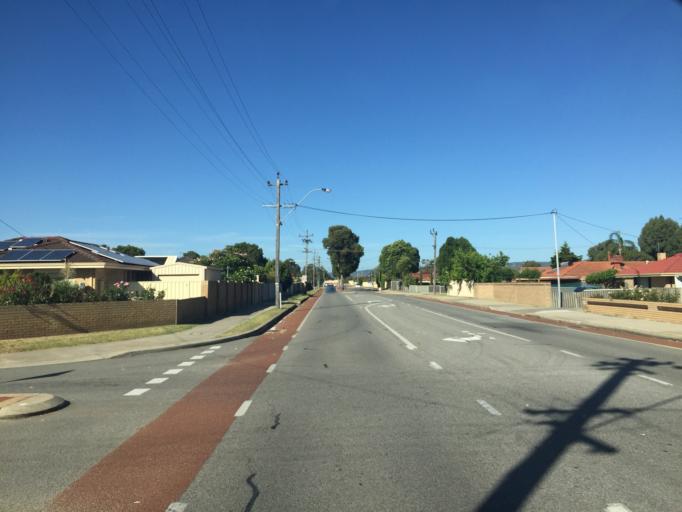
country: AU
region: Western Australia
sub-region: Canning
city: East Cannington
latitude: -32.0106
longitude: 115.9689
